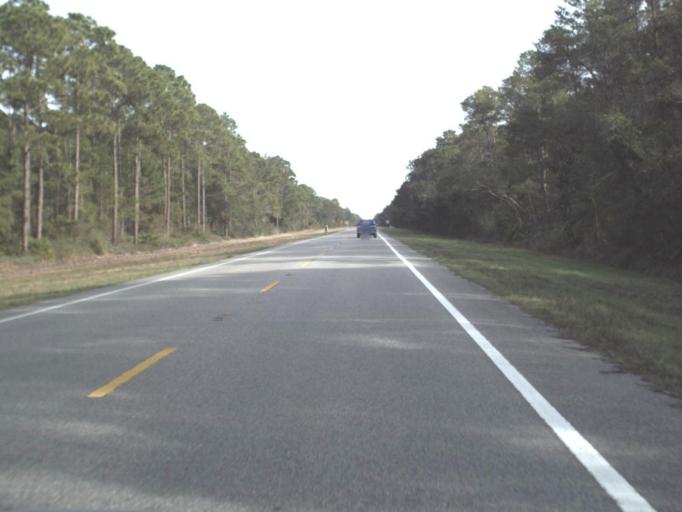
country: US
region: Florida
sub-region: Bay County
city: Mexico Beach
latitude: 29.9674
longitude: -85.4513
